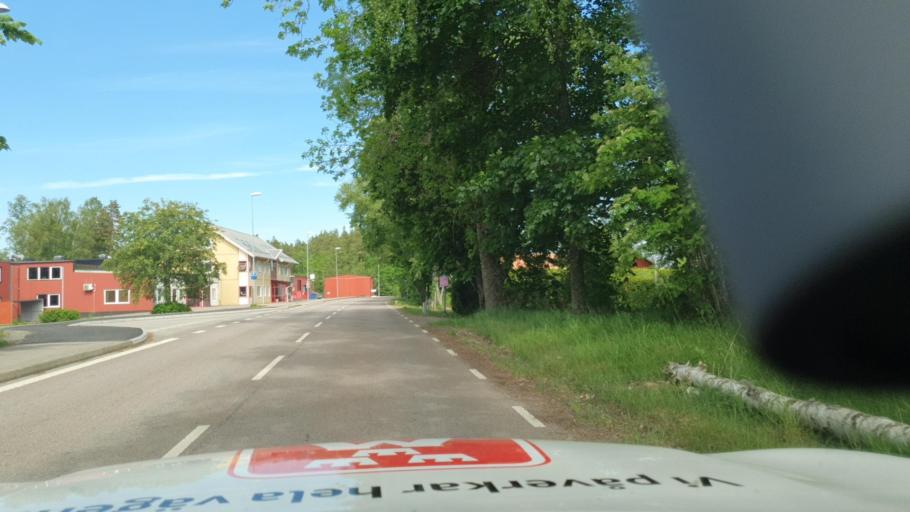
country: SE
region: Vaestra Goetaland
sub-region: Essunga Kommun
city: Nossebro
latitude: 58.2344
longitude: 12.6698
